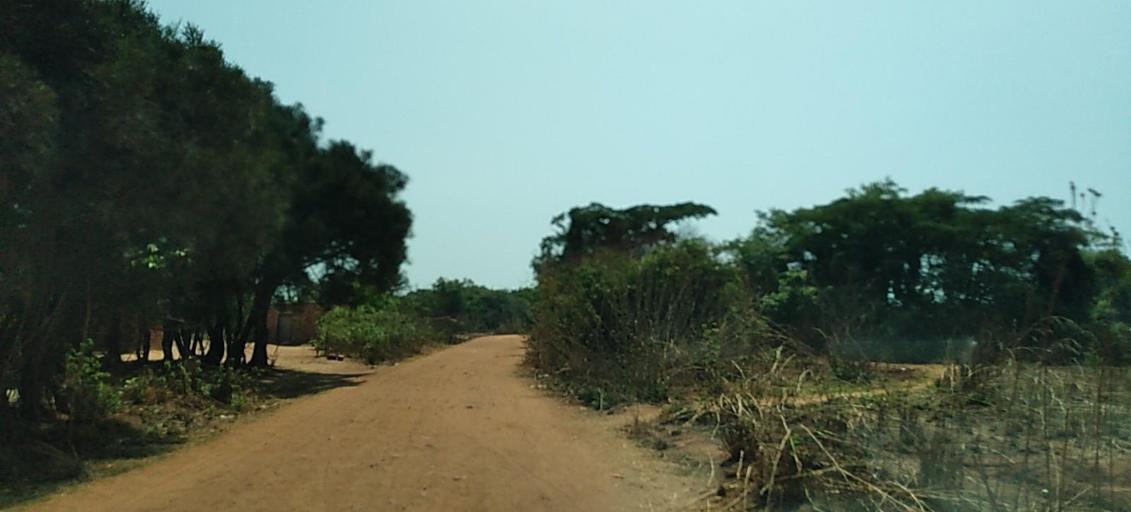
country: ZM
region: Copperbelt
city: Luanshya
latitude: -13.3493
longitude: 28.4013
